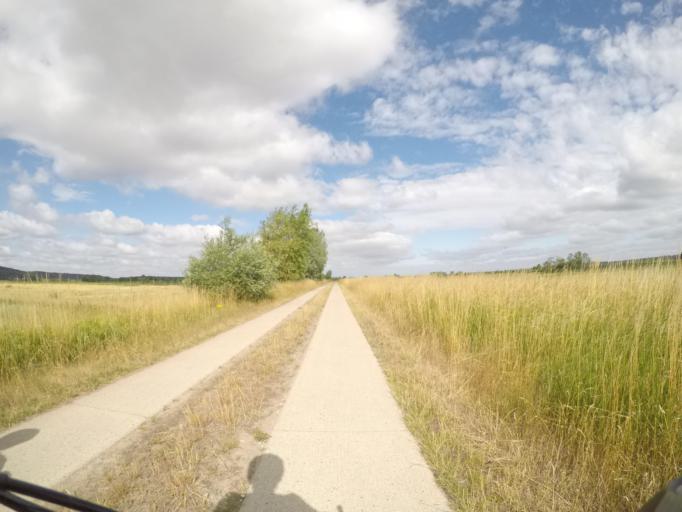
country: DE
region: Lower Saxony
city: Hitzacker
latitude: 53.1700
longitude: 11.0598
